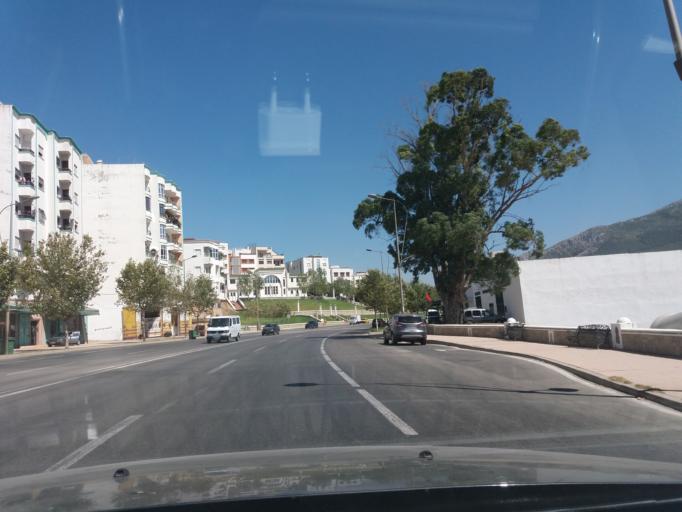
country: MA
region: Tanger-Tetouan
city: Tetouan
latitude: 35.5672
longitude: -5.4048
